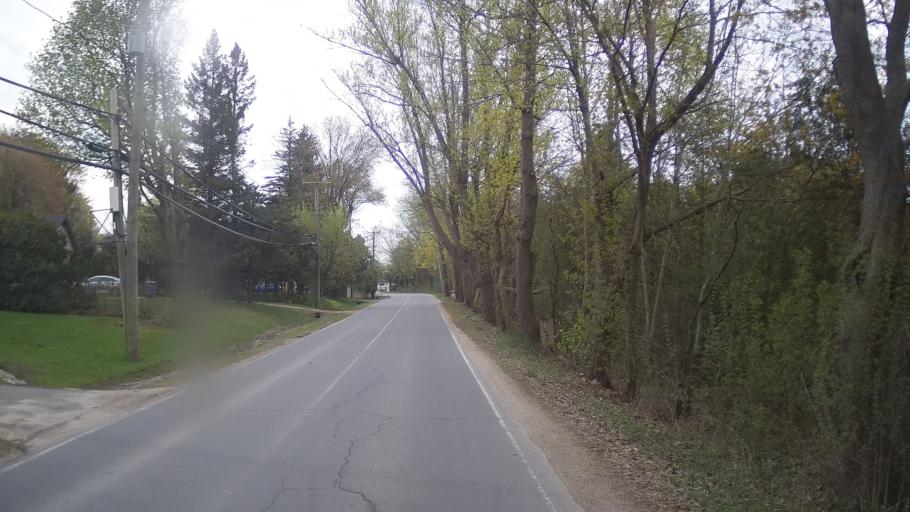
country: CA
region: Quebec
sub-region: Monteregie
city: Hudson
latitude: 45.4481
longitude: -74.1665
